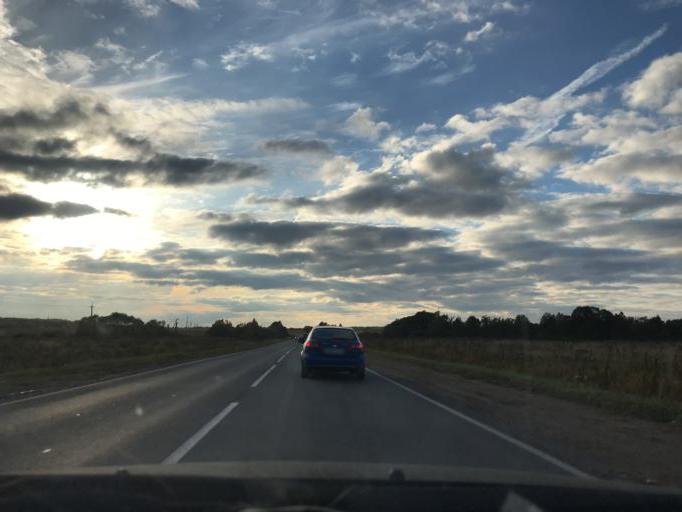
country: RU
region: Kaluga
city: Kurovskoye
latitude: 54.5285
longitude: 35.9223
